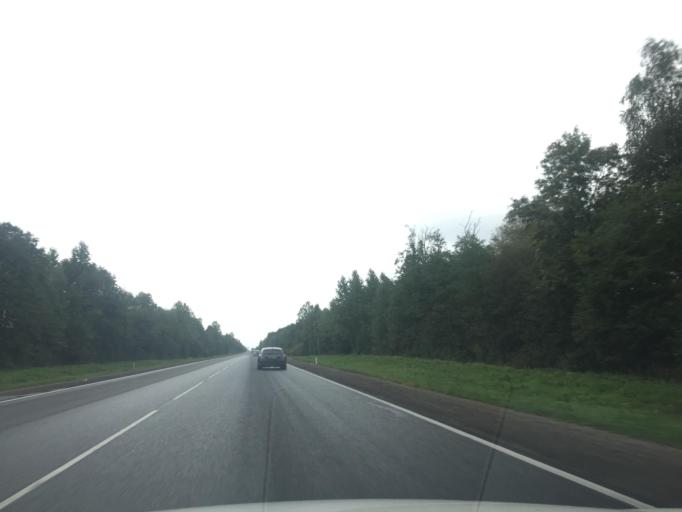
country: RU
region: Leningrad
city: Rozhdestveno
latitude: 59.3595
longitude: 29.9629
